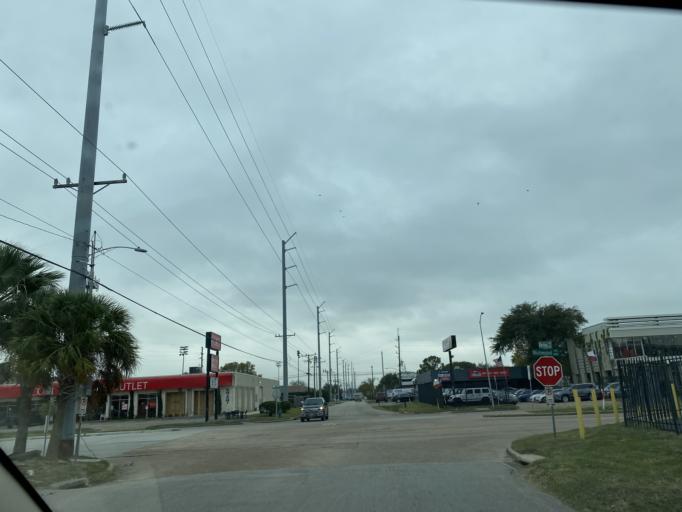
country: US
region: Texas
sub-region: Harris County
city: Bellaire
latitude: 29.7319
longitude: -95.4804
